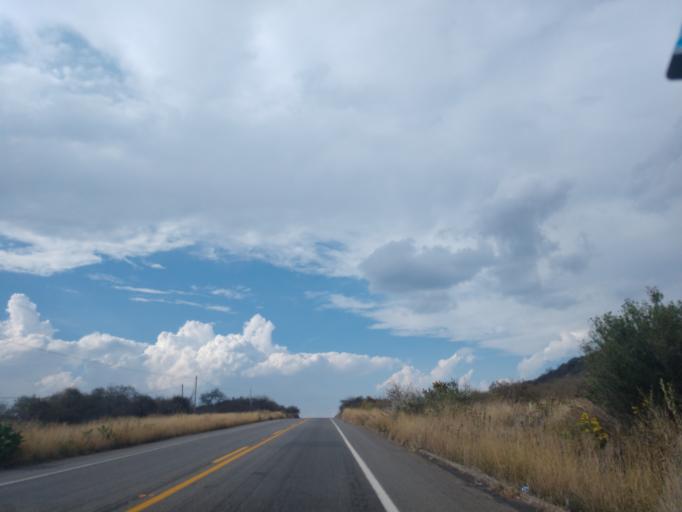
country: MX
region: Jalisco
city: La Manzanilla de la Paz
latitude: 20.0931
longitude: -103.1679
